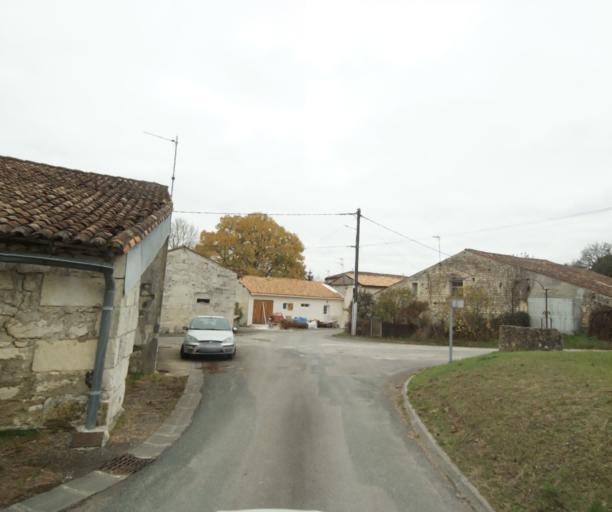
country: FR
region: Poitou-Charentes
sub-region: Departement de la Charente-Maritime
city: Les Gonds
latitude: 45.7210
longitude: -0.6297
